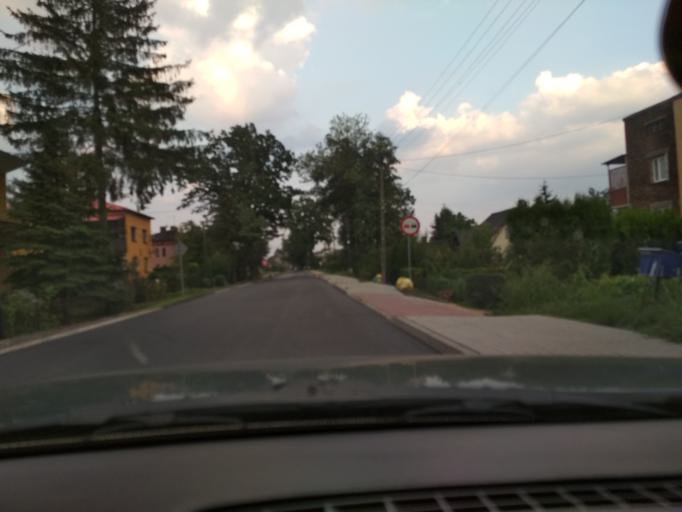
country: PL
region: Silesian Voivodeship
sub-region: Powiat cieszynski
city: Mnich
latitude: 49.8973
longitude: 18.7978
